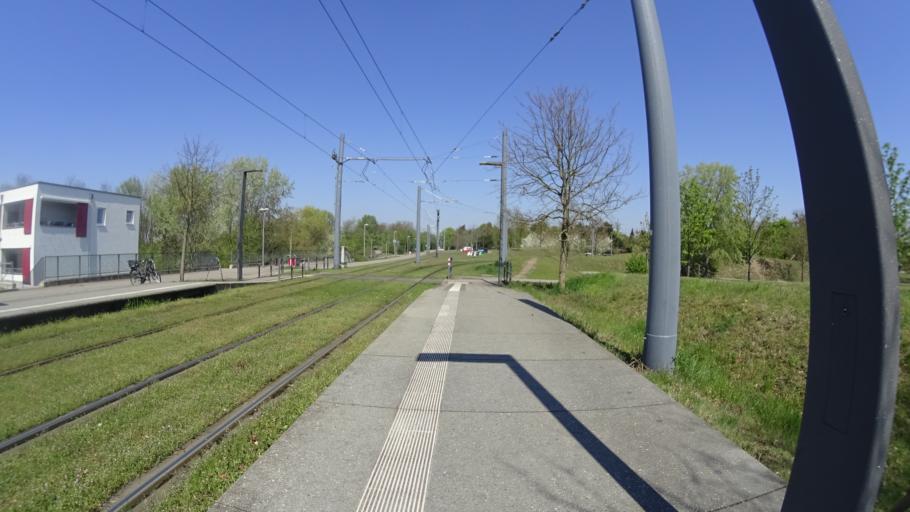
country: DE
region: Baden-Wuerttemberg
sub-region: Karlsruhe Region
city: Karlsruhe
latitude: 49.0366
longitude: 8.3882
